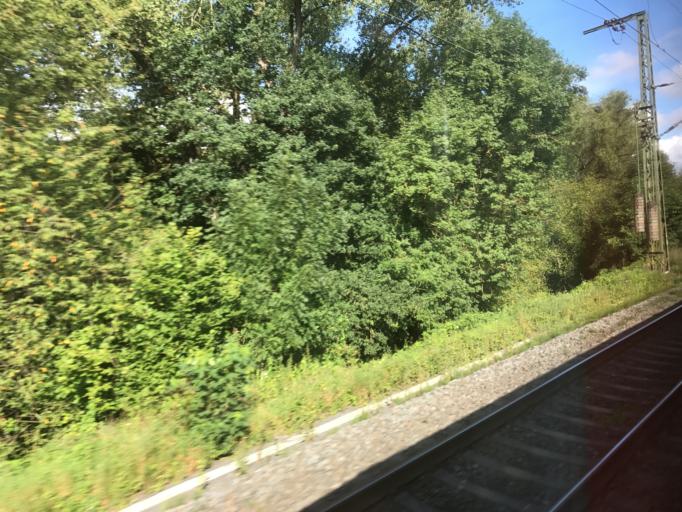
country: DE
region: Hesse
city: Staufenberg
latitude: 50.6665
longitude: 8.7125
